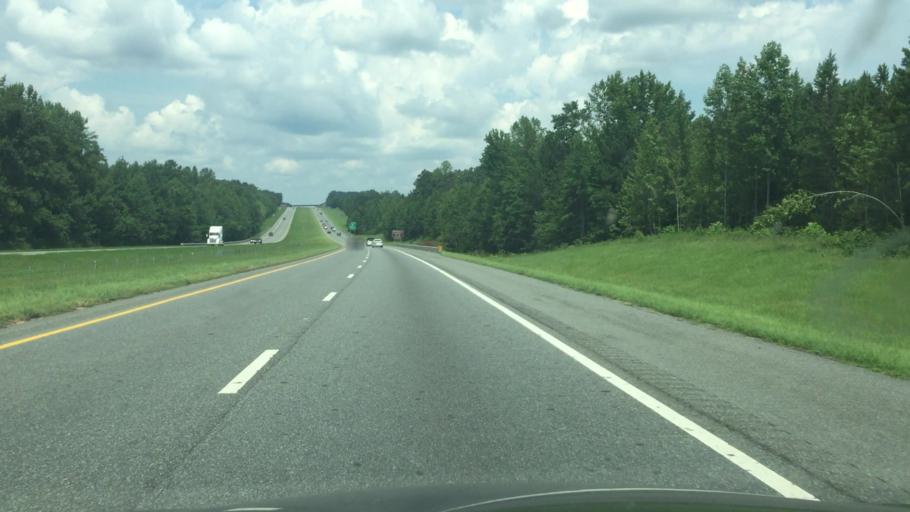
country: US
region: North Carolina
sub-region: Montgomery County
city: Biscoe
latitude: 35.5204
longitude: -79.7828
